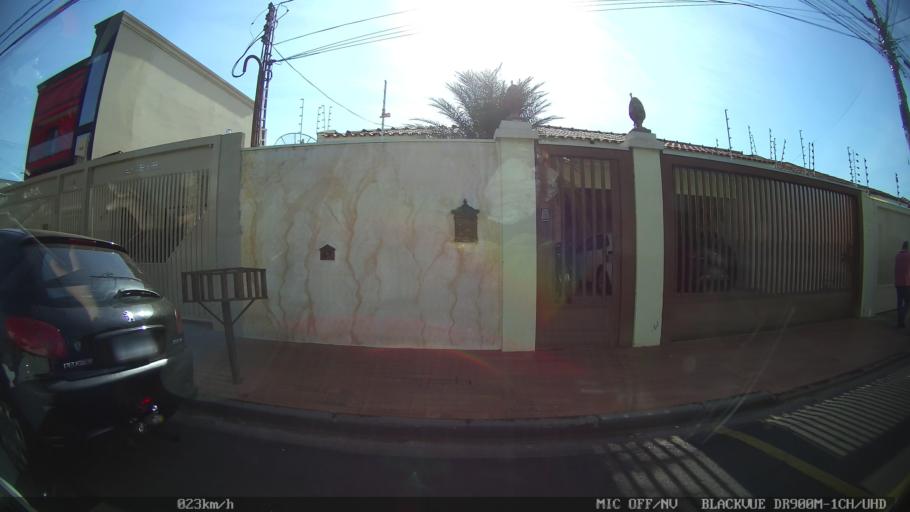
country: BR
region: Sao Paulo
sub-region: Sao Jose Do Rio Preto
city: Sao Jose do Rio Preto
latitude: -20.8034
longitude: -49.3899
